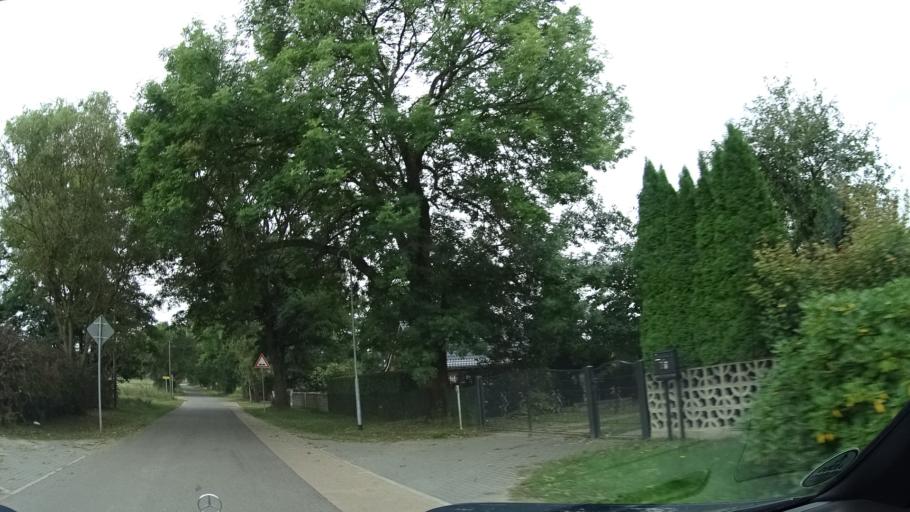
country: DE
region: Brandenburg
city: Neuruppin
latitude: 52.9589
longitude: 12.7615
